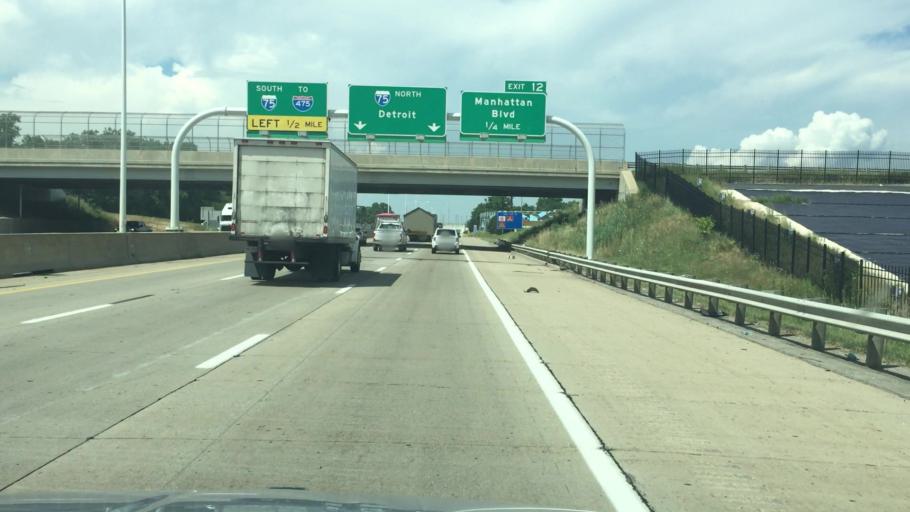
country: US
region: Ohio
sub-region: Lucas County
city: Toledo
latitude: 41.6784
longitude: -83.5155
